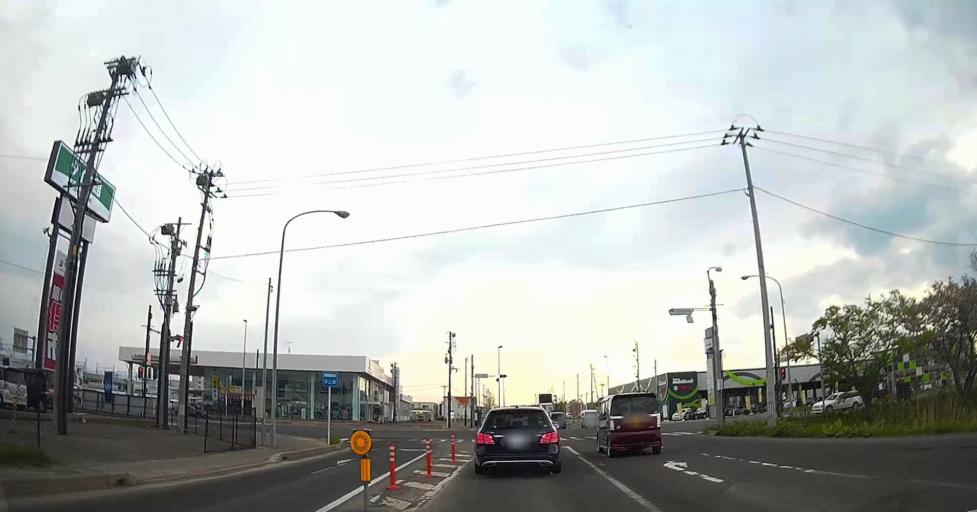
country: JP
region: Aomori
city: Aomori Shi
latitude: 40.8338
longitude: 140.6905
